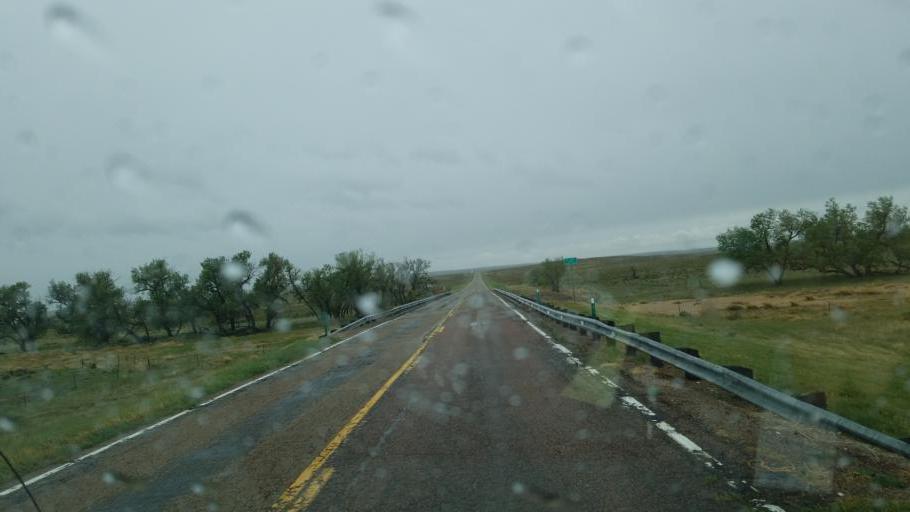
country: US
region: Colorado
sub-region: Lincoln County
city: Hugo
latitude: 38.8586
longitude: -103.1472
